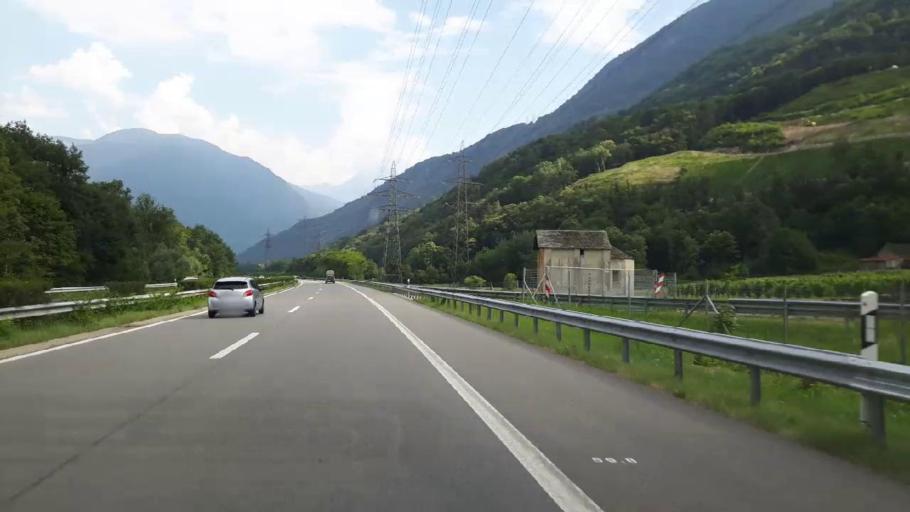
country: CH
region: Ticino
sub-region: Riviera District
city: Claro
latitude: 46.2498
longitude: 9.0110
